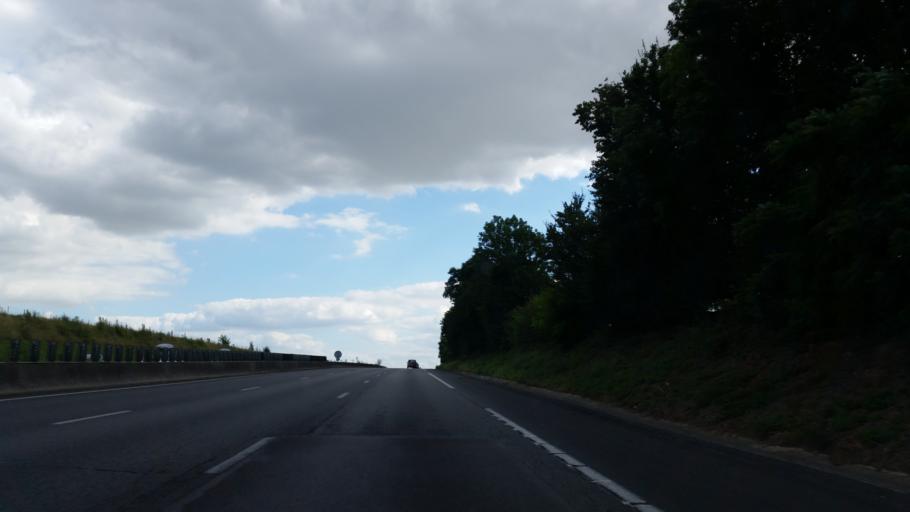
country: FR
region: Nord-Pas-de-Calais
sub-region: Departement du Pas-de-Calais
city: Croisilles
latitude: 50.1888
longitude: 2.8725
